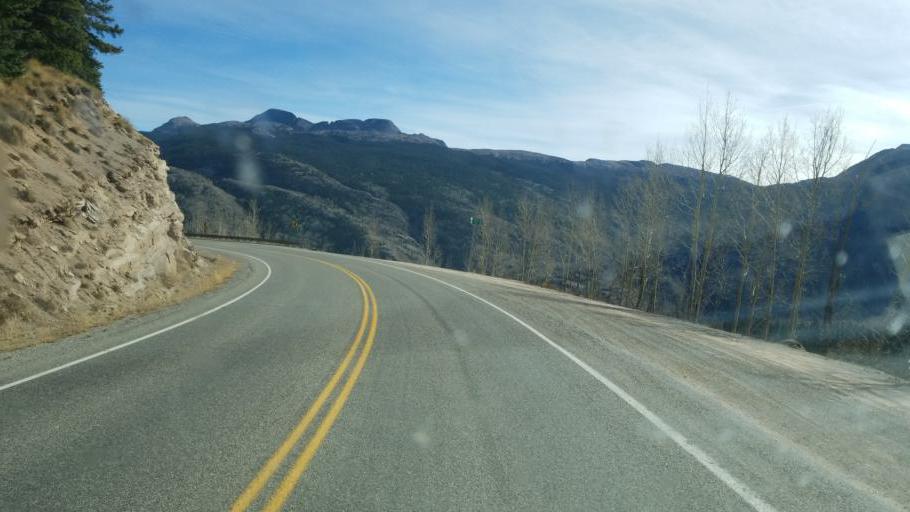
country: US
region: Colorado
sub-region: San Juan County
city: Silverton
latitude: 37.7007
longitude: -107.7707
